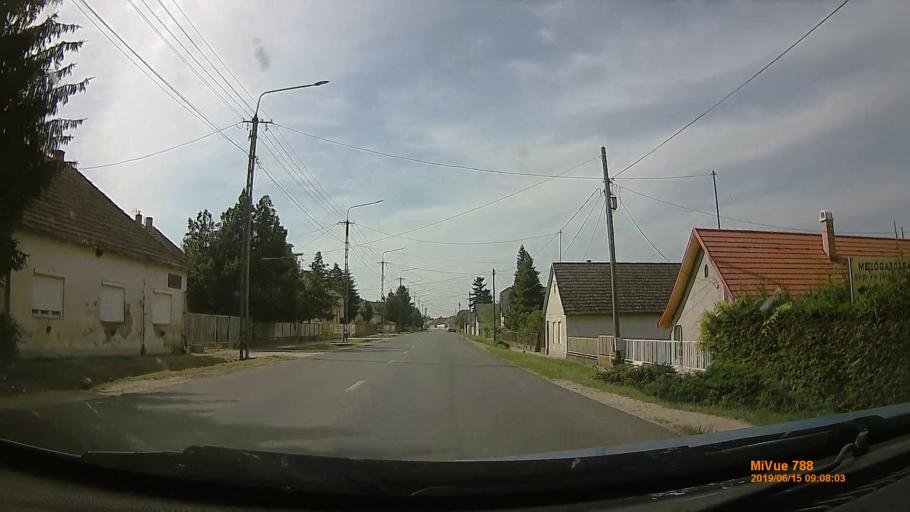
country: HU
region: Tolna
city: Iregszemcse
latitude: 46.6993
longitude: 18.1804
